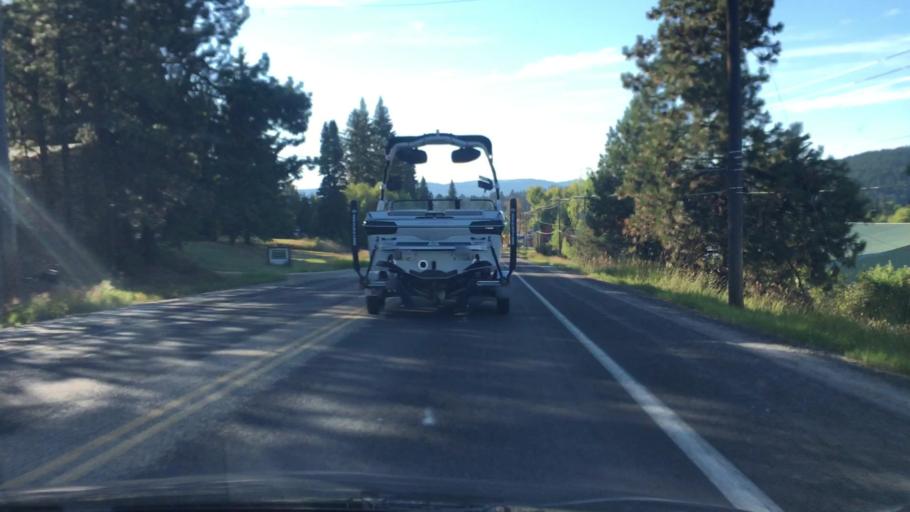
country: US
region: Idaho
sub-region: Valley County
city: Cascade
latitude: 44.5104
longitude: -116.0362
